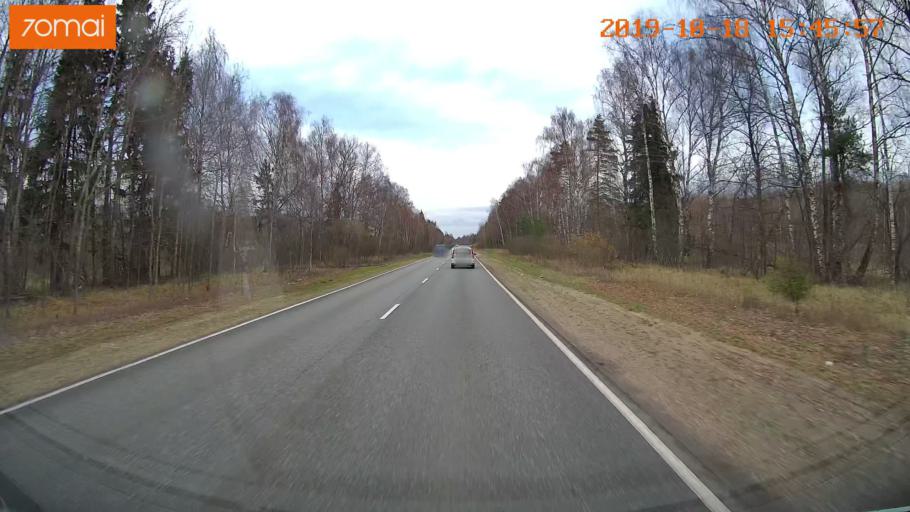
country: RU
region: Vladimir
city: Golovino
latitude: 56.0008
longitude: 40.5654
